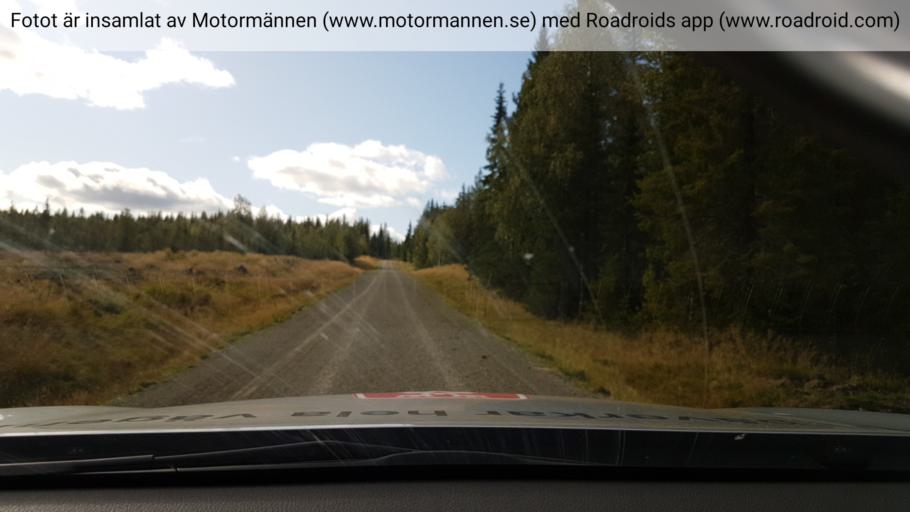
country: SE
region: Vaesterbotten
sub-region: Mala Kommun
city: Mala
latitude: 65.4690
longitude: 18.1865
